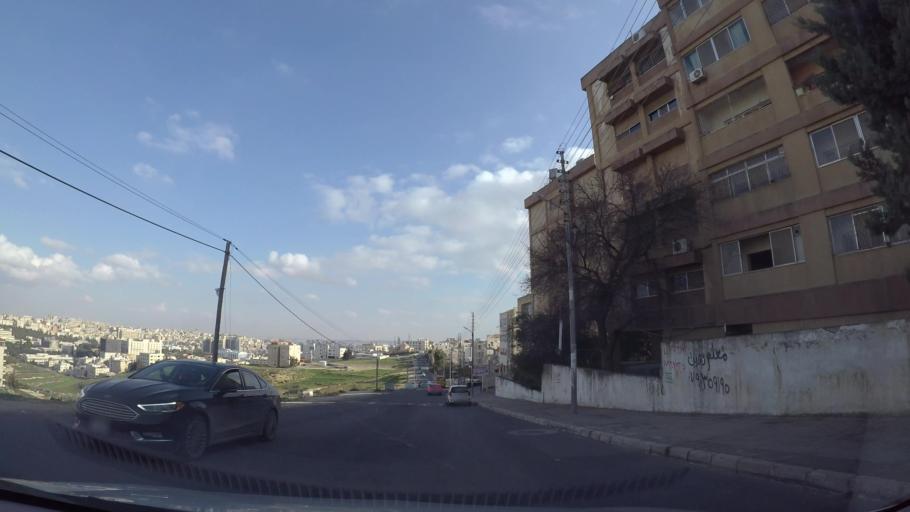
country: JO
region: Amman
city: Al Jubayhah
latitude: 32.0104
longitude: 35.8638
